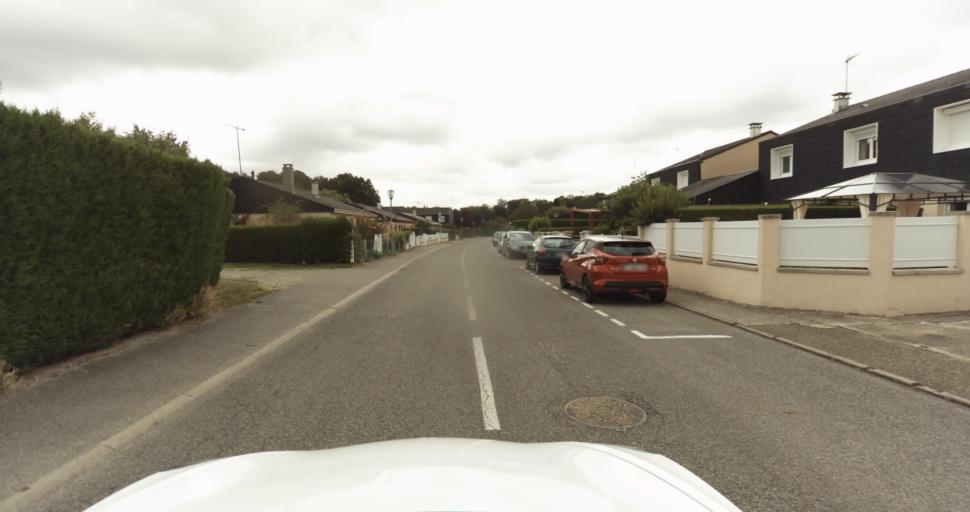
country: FR
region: Haute-Normandie
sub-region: Departement de l'Eure
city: Saint-Sebastien-de-Morsent
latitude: 49.0050
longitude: 1.0863
